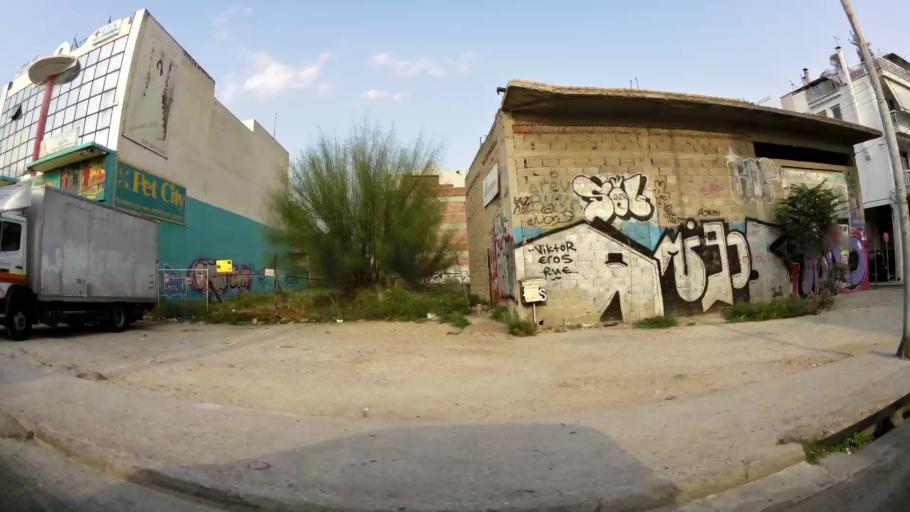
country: GR
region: Attica
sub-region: Nomarchia Athinas
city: Ilion
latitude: 38.0359
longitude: 23.6943
